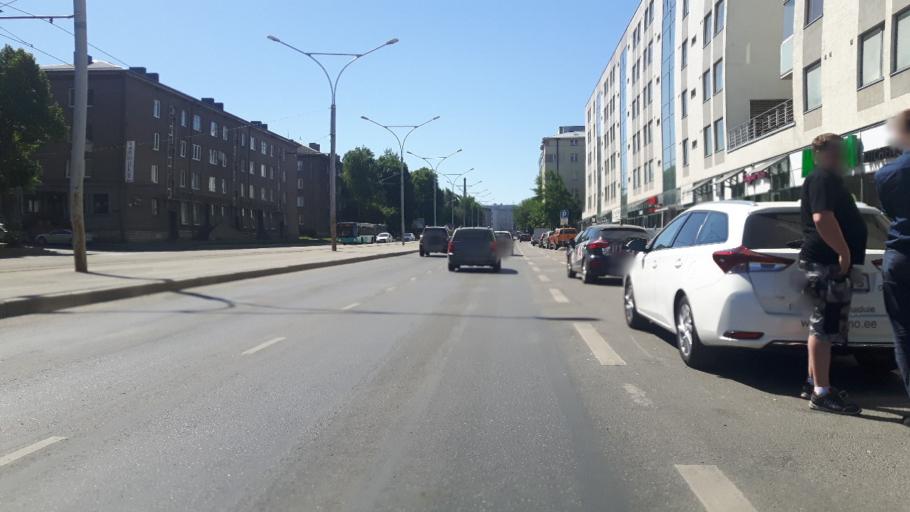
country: EE
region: Harju
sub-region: Tallinna linn
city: Tallinn
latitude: 59.4143
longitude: 24.7391
